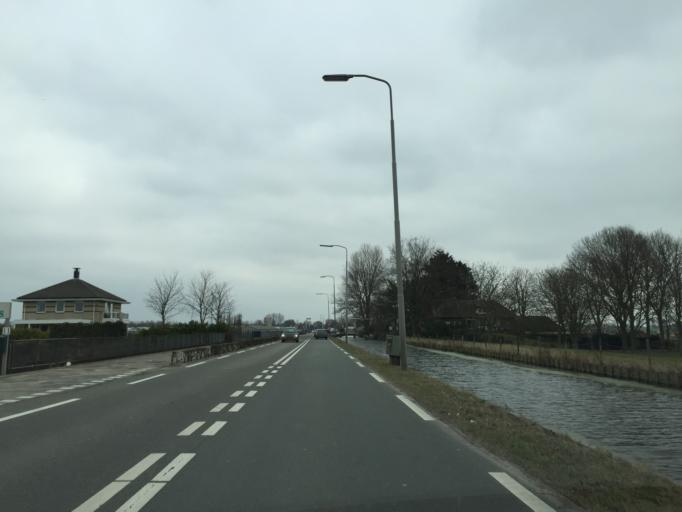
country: NL
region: South Holland
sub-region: Gemeente Pijnacker-Nootdorp
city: Pijnacker
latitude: 52.0305
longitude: 4.4394
